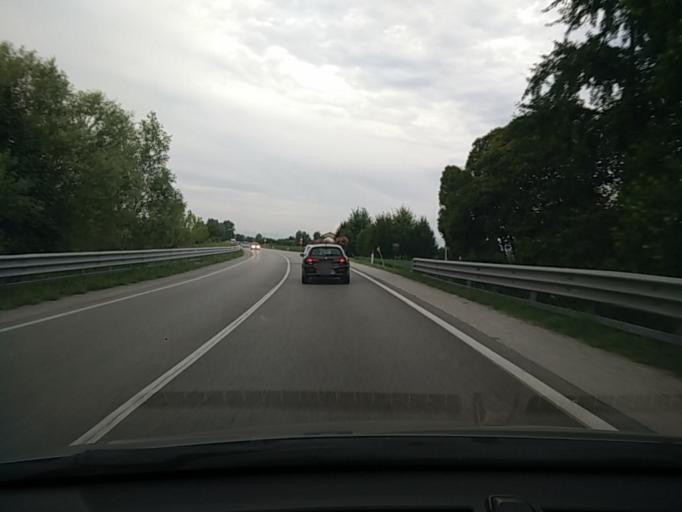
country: IT
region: Veneto
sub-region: Provincia di Venezia
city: Passarella
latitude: 45.5714
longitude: 12.5628
